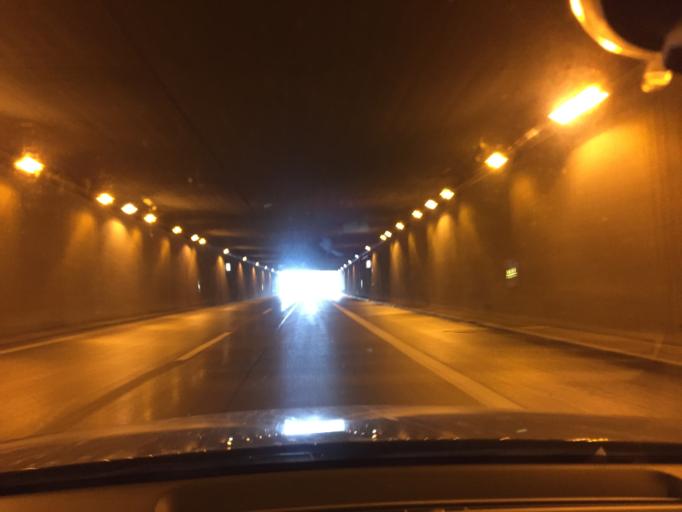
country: DE
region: Saxony
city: Liebstadt
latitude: 50.7859
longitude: 13.8944
